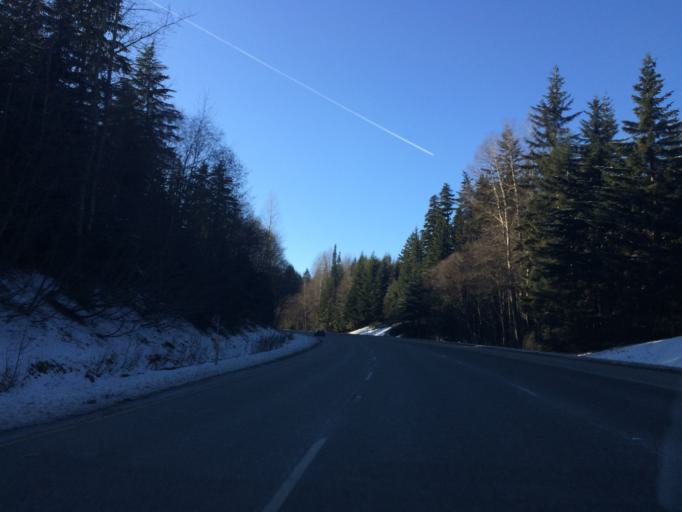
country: US
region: Washington
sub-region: Kittitas County
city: Cle Elum
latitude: 47.2701
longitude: -121.2337
